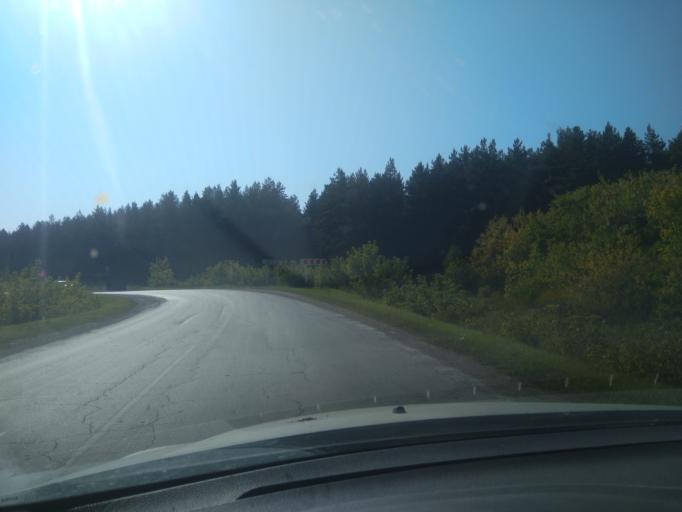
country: RU
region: Sverdlovsk
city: Pokrovskoye
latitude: 56.4538
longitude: 61.6023
